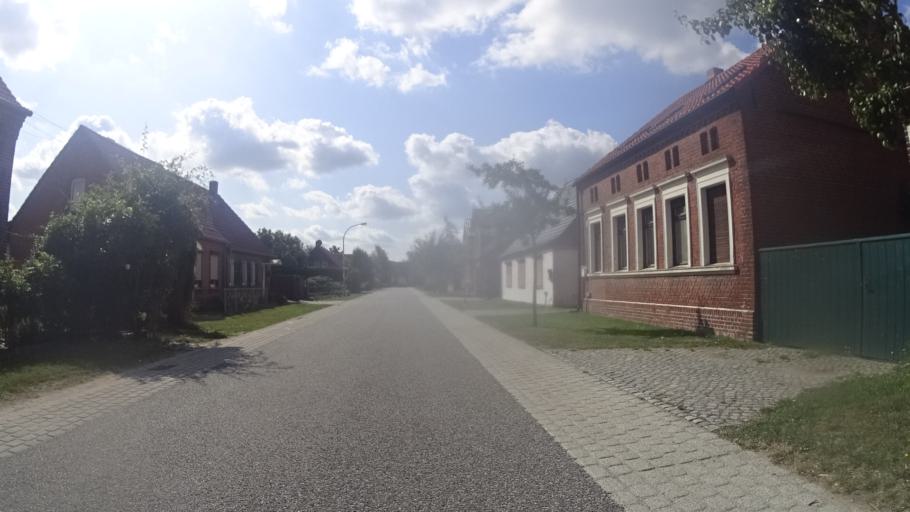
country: DE
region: Brandenburg
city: Ruhstadt
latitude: 52.9223
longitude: 11.8705
